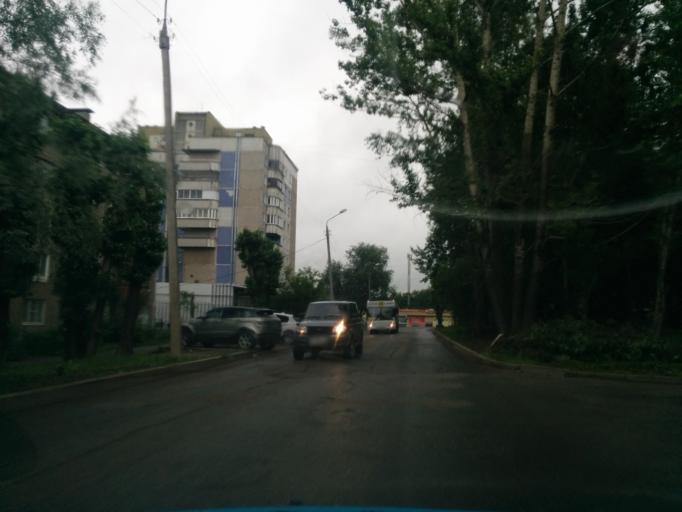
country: RU
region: Perm
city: Perm
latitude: 57.9908
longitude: 56.2326
